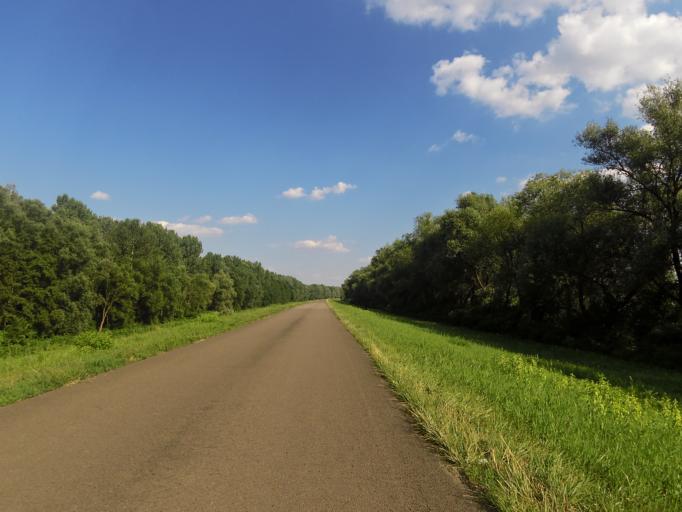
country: HU
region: Jasz-Nagykun-Szolnok
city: Abadszalok
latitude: 47.5108
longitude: 20.5891
